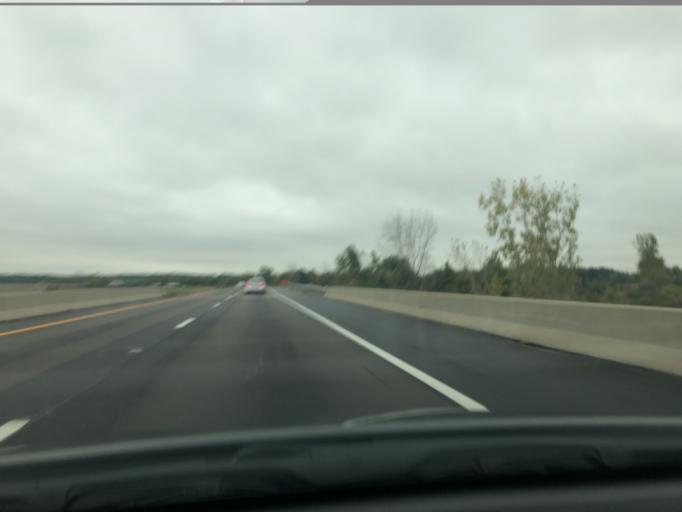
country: US
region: Ohio
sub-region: Union County
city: Marysville
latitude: 40.2389
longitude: -83.4103
